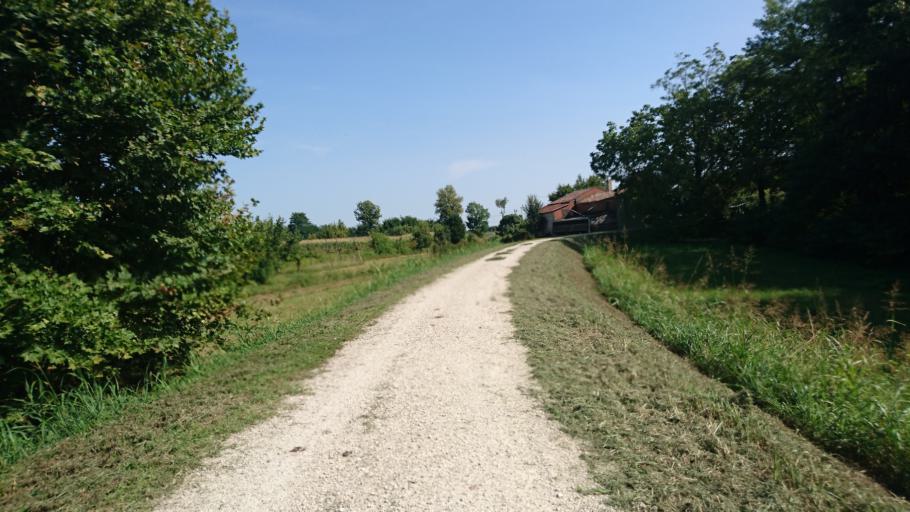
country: IT
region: Veneto
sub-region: Provincia di Padova
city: Veggiano
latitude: 45.4421
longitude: 11.7253
